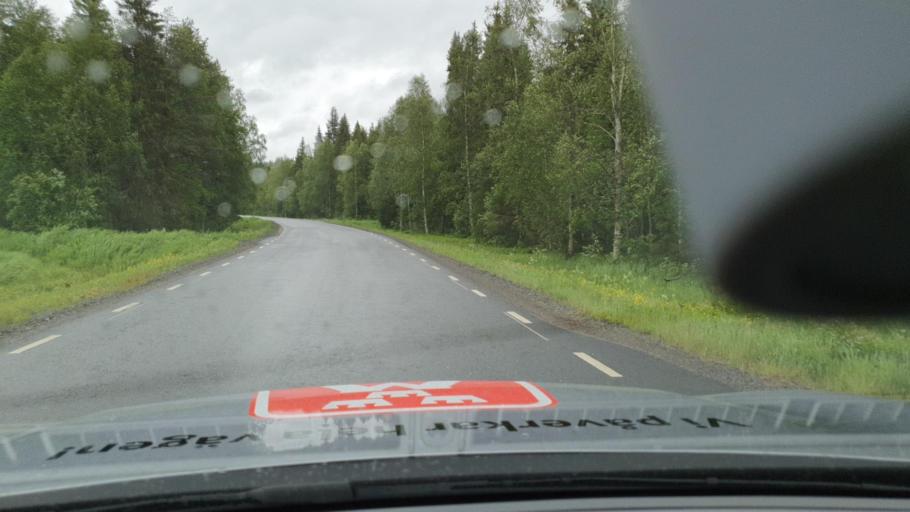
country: FI
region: Lapland
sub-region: Torniolaakso
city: Ylitornio
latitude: 66.1847
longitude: 23.7283
